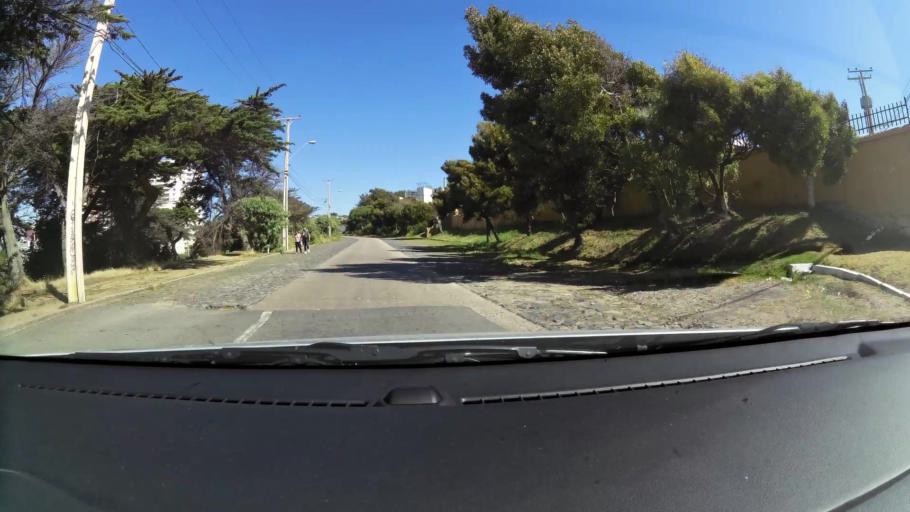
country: CL
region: Valparaiso
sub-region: Provincia de Valparaiso
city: Valparaiso
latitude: -33.0224
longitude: -71.6457
